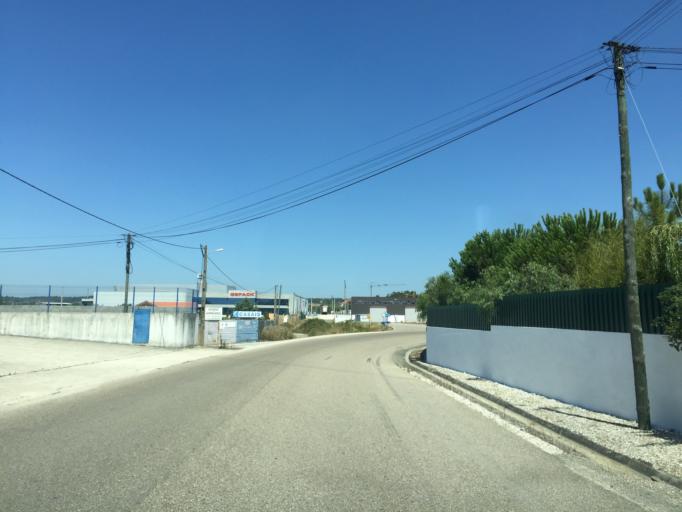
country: PT
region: Lisbon
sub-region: Azambuja
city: Aveiras de Cima
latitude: 39.1473
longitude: -8.9011
